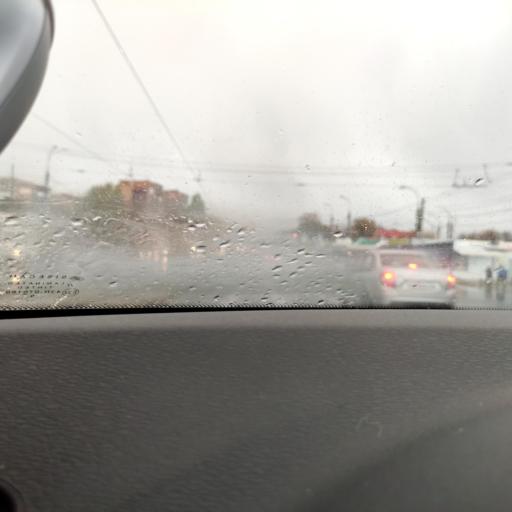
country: RU
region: Samara
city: Smyshlyayevka
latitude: 53.2107
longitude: 50.2732
